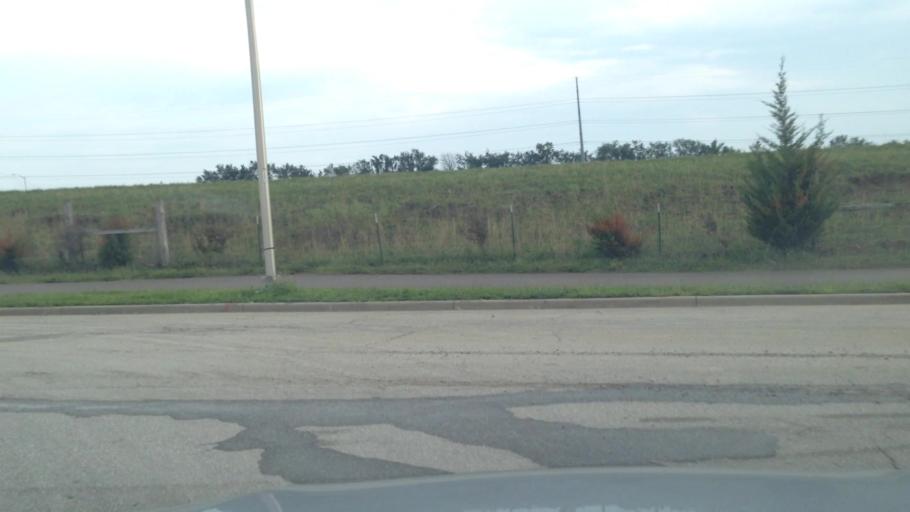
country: US
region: Kansas
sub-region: Johnson County
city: Olathe
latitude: 38.9364
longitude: -94.7990
